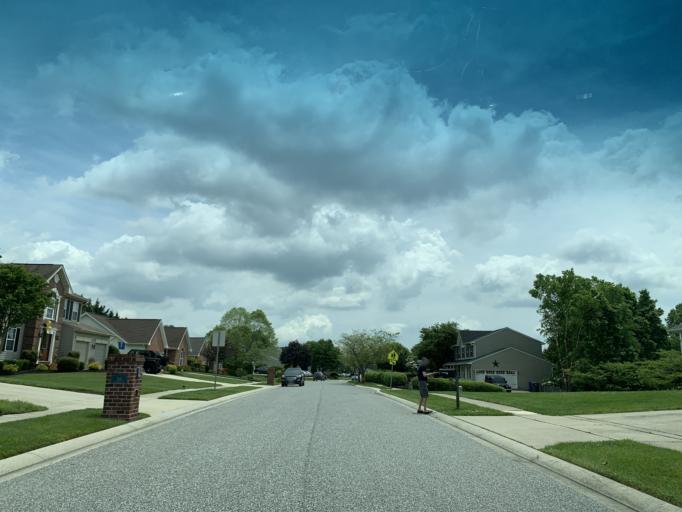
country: US
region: Maryland
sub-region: Harford County
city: South Bel Air
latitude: 39.5430
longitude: -76.3049
